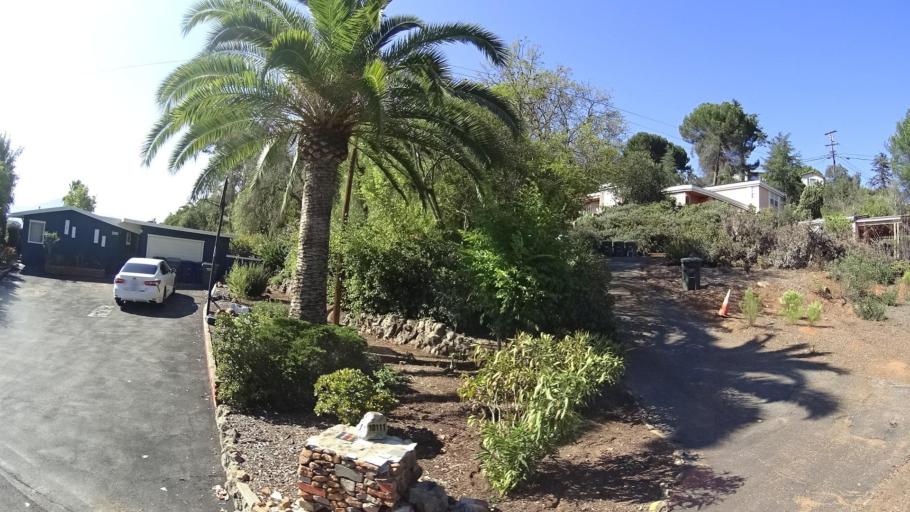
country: US
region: California
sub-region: San Diego County
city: Casa de Oro-Mount Helix
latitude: 32.7693
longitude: -116.9800
